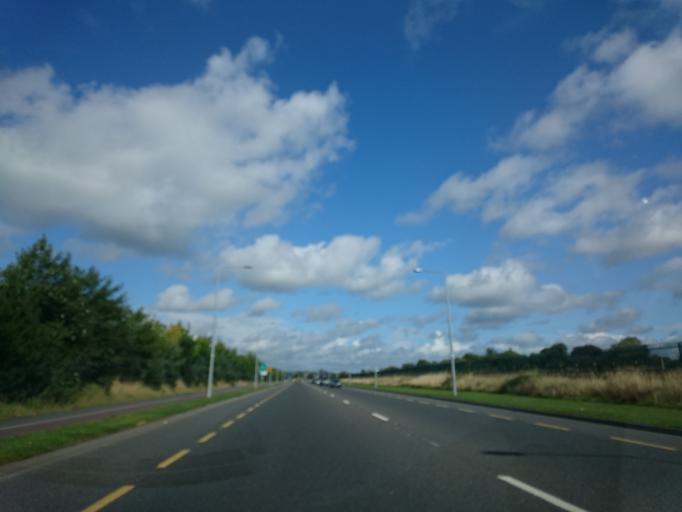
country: IE
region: Leinster
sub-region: Kilkenny
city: Kilkenny
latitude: 52.6607
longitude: -7.2263
